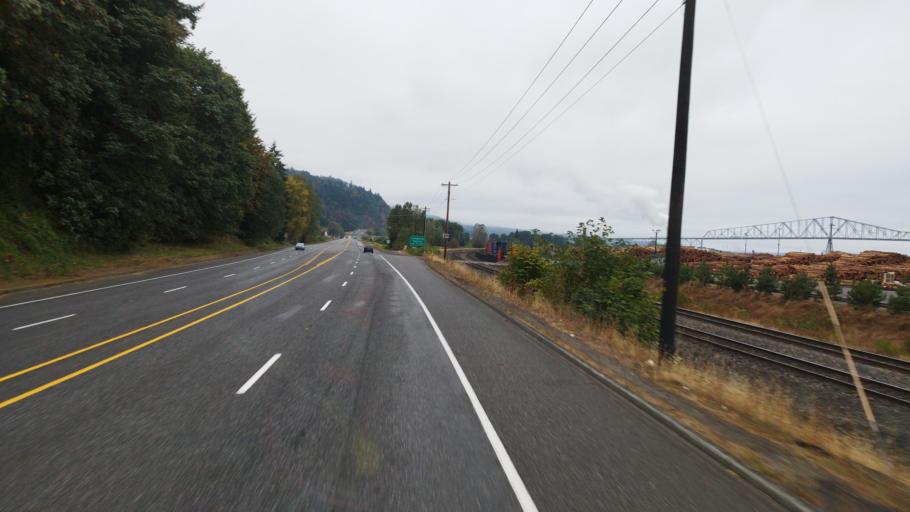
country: US
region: Oregon
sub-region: Columbia County
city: Rainier
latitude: 46.0938
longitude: -122.9500
